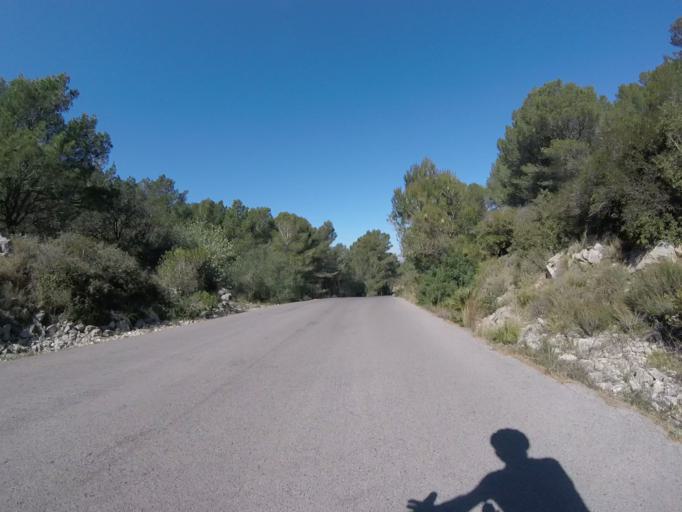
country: ES
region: Valencia
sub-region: Provincia de Castello
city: Cervera del Maestre
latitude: 40.4073
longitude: 0.1971
